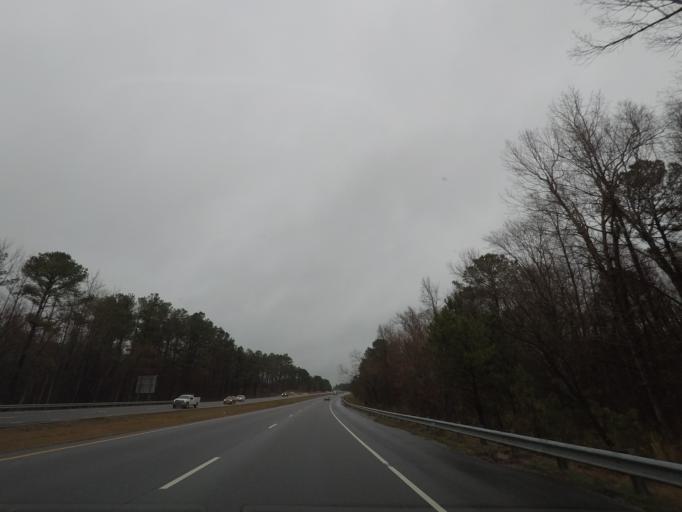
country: US
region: North Carolina
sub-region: Lee County
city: Broadway
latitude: 35.3273
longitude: -79.0935
